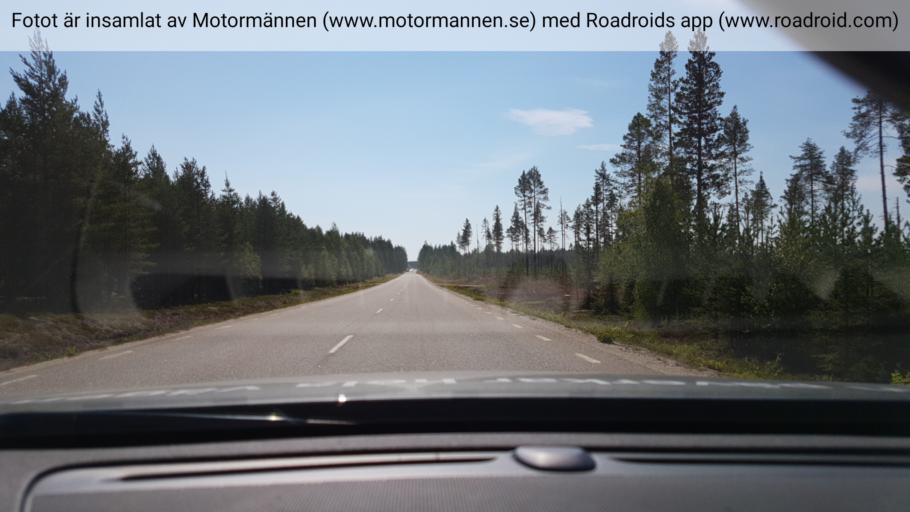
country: SE
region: Vaesterbotten
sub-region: Norsjo Kommun
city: Norsjoe
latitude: 64.5502
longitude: 19.3284
